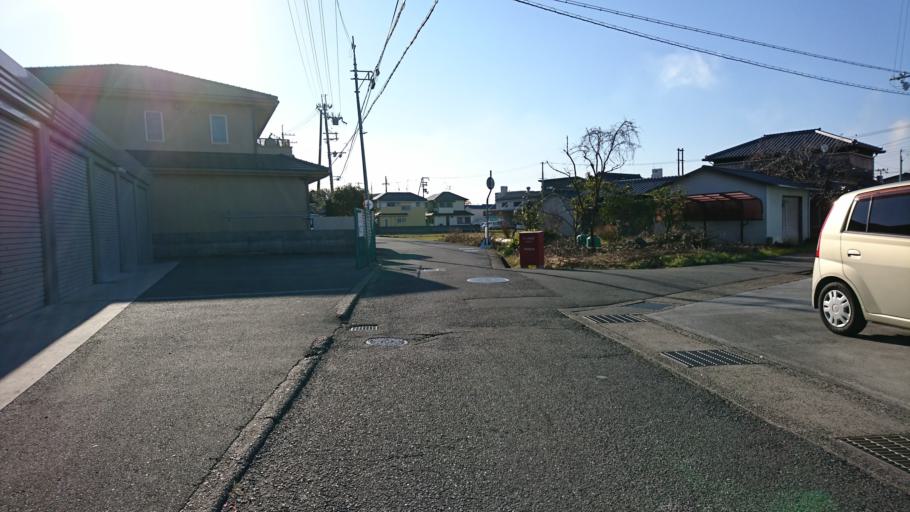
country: JP
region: Hyogo
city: Kakogawacho-honmachi
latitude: 34.7393
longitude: 134.8503
